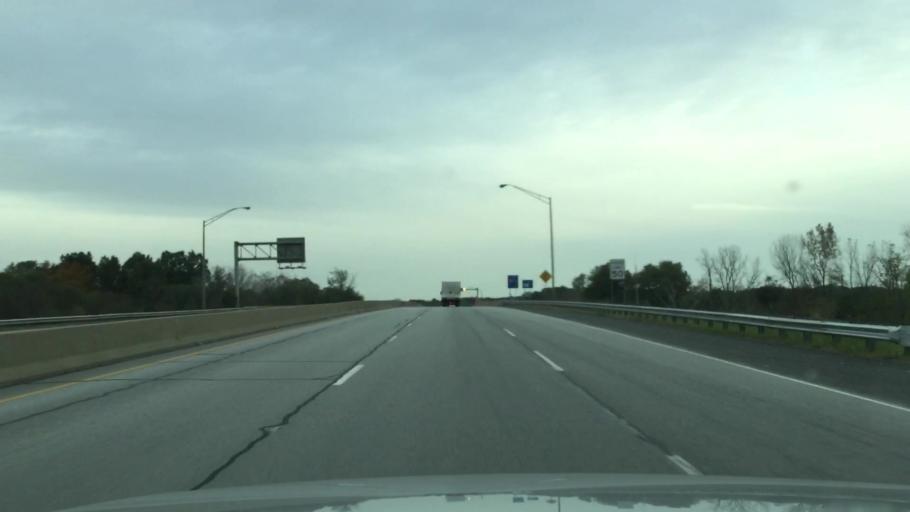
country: US
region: Indiana
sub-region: Porter County
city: Chesterton
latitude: 41.6214
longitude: -87.0441
